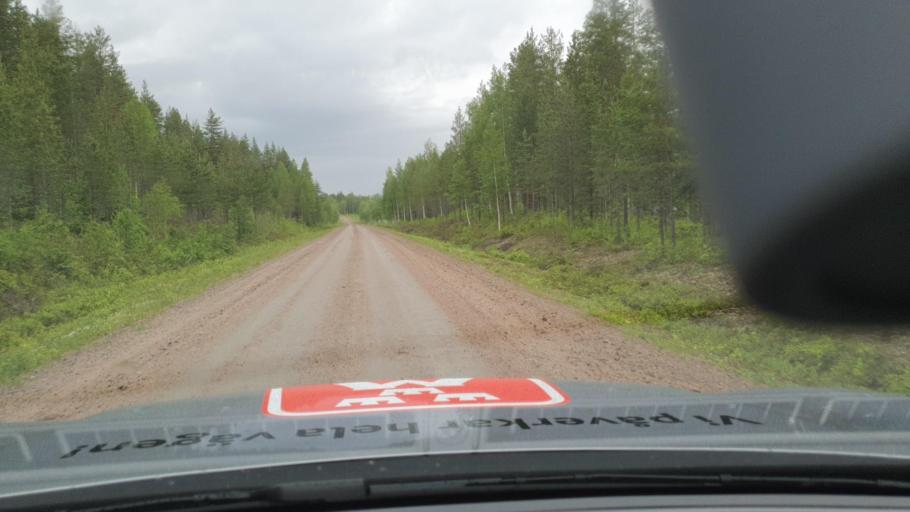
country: SE
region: Norrbotten
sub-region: Overkalix Kommun
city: OEverkalix
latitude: 66.6021
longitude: 22.7481
